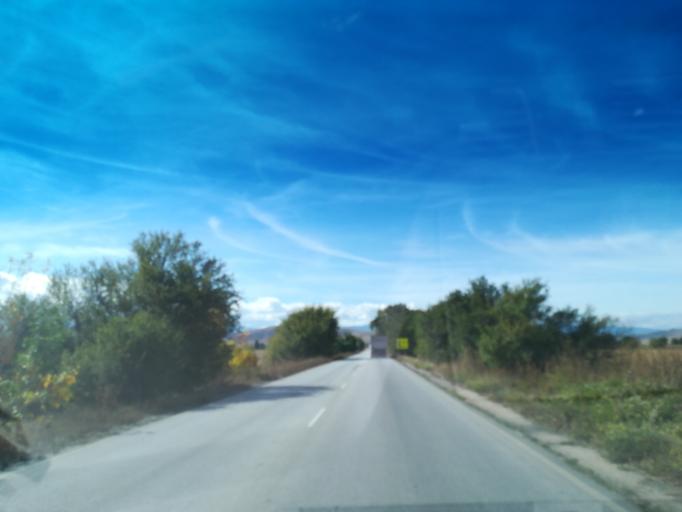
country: BG
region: Plovdiv
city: Stamboliyski
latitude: 42.1121
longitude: 24.5178
